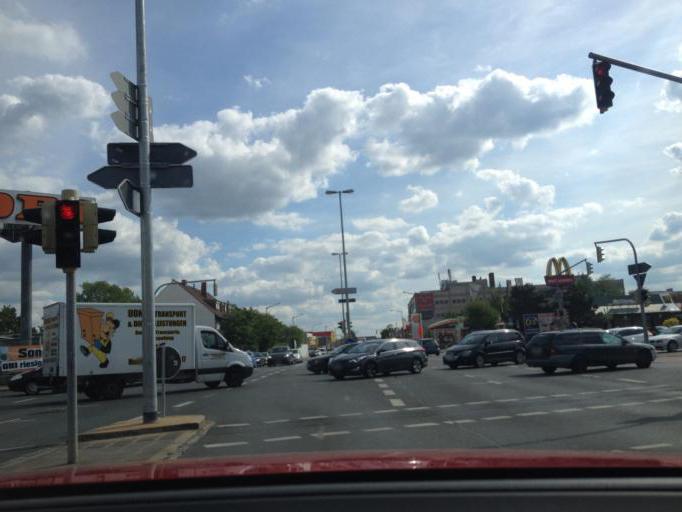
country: DE
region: Bavaria
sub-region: Regierungsbezirk Mittelfranken
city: Grossreuth bei Schweinau
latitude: 49.4539
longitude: 11.0161
